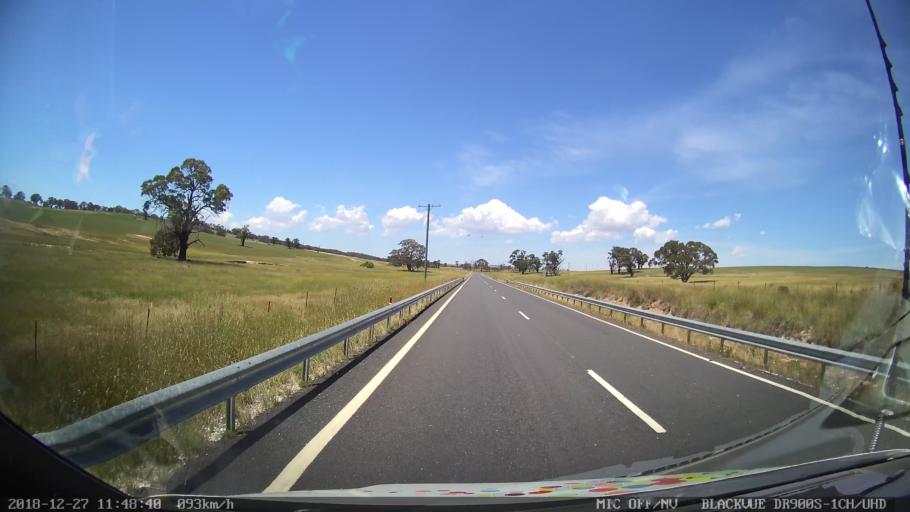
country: AU
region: New South Wales
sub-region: Bathurst Regional
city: Perthville
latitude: -33.6092
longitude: 149.4355
